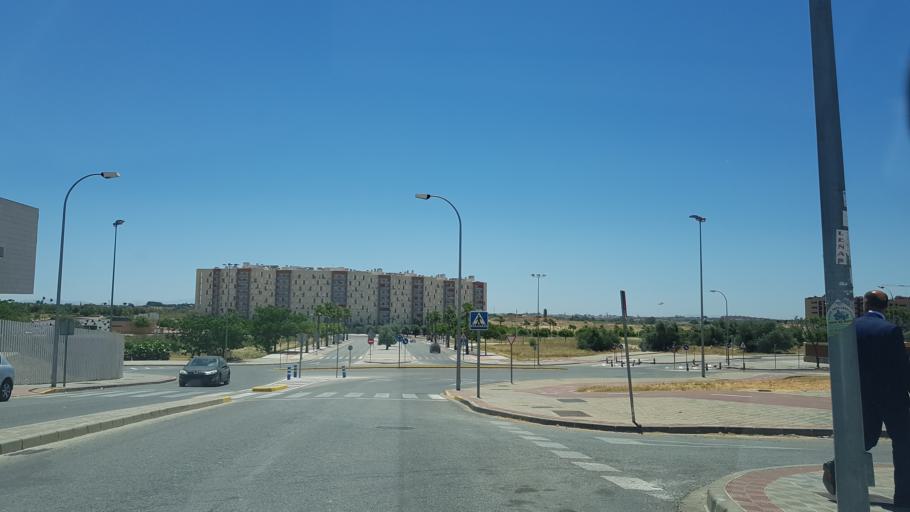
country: ES
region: Andalusia
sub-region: Provincia de Sevilla
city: Dos Hermanas
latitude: 37.3252
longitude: -5.9265
